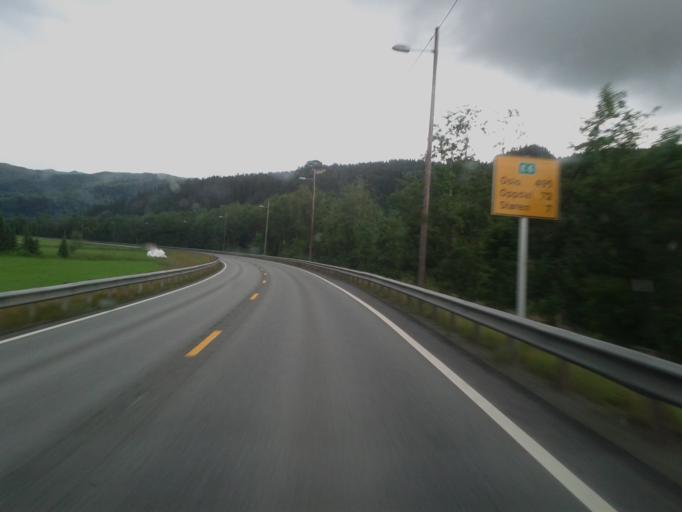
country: NO
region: Sor-Trondelag
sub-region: Melhus
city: Lundamo
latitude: 63.1027
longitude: 10.2336
